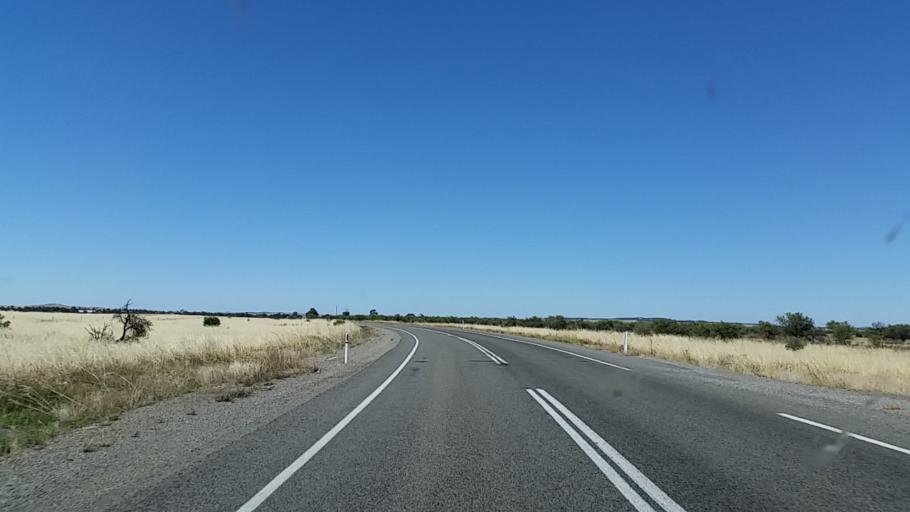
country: AU
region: South Australia
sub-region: Peterborough
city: Peterborough
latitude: -33.1704
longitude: 138.9126
